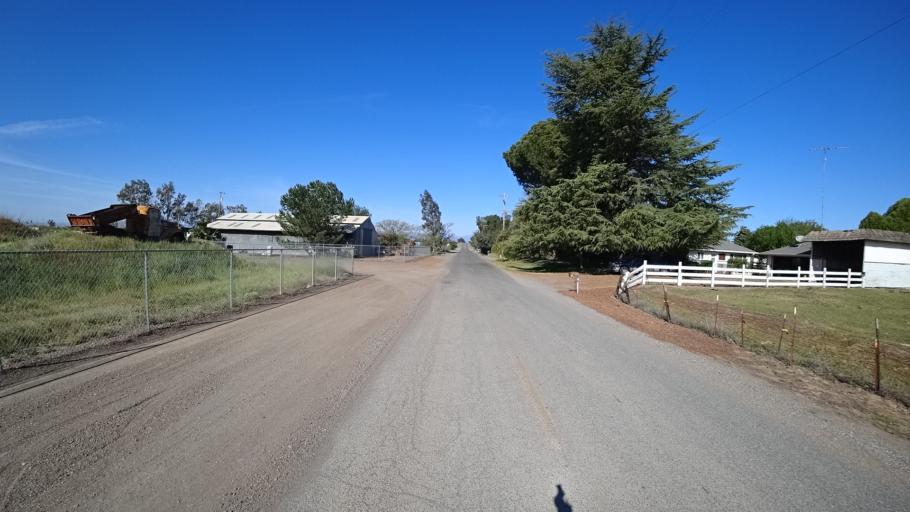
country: US
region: California
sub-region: Glenn County
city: Orland
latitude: 39.7112
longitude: -122.1999
